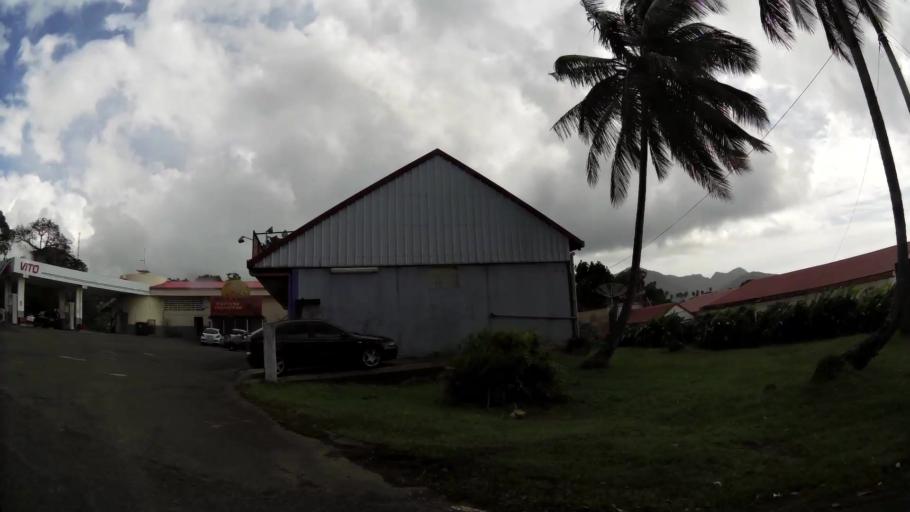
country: GP
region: Guadeloupe
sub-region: Guadeloupe
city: Saint-Claude
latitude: 16.0091
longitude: -61.7102
